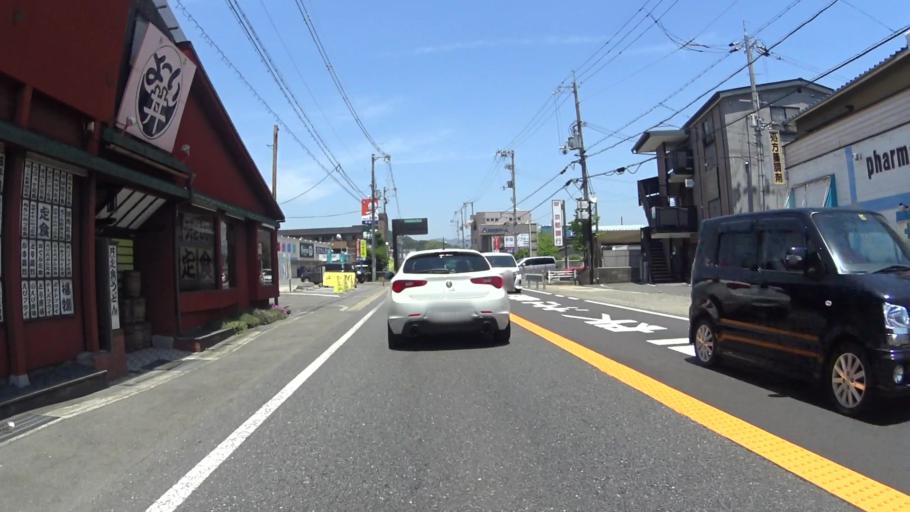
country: JP
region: Kyoto
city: Kameoka
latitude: 35.0469
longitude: 135.5455
